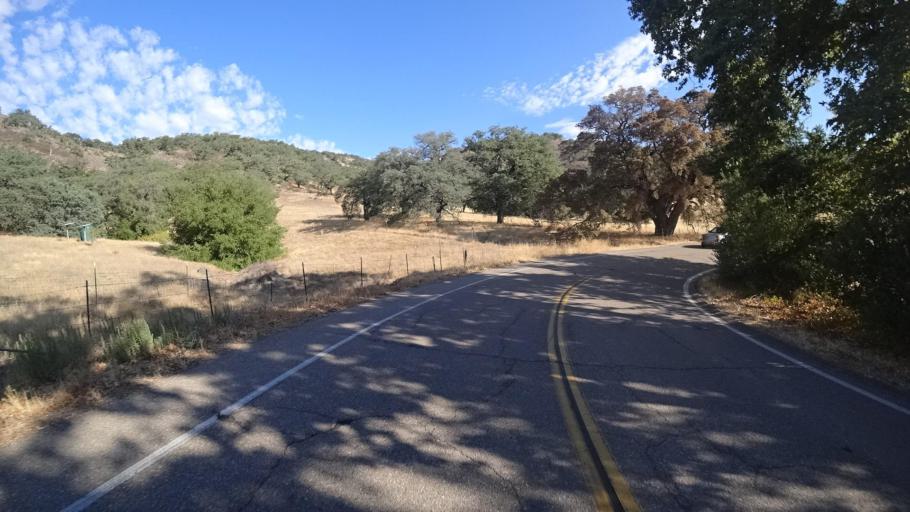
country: US
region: California
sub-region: San Diego County
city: Julian
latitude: 33.1504
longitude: -116.6965
